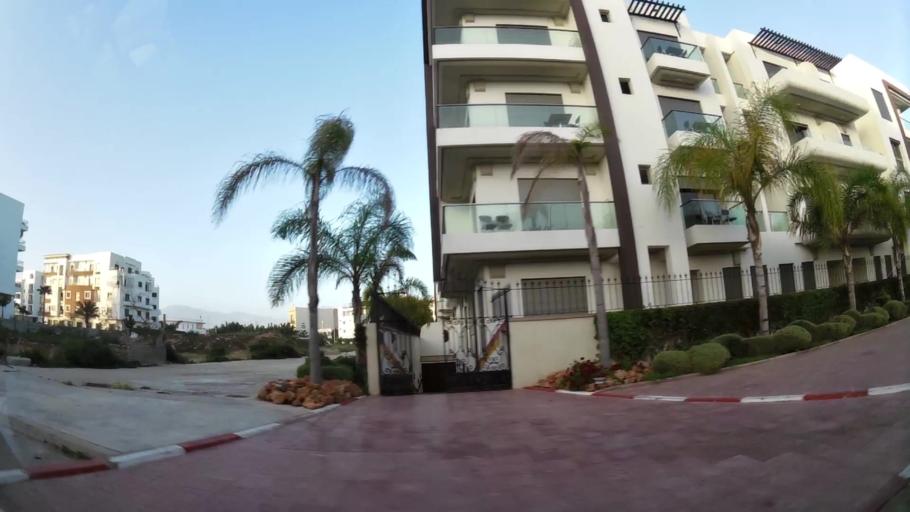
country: MA
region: Souss-Massa-Draa
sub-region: Agadir-Ida-ou-Tnan
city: Agadir
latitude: 30.4002
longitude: -9.5908
